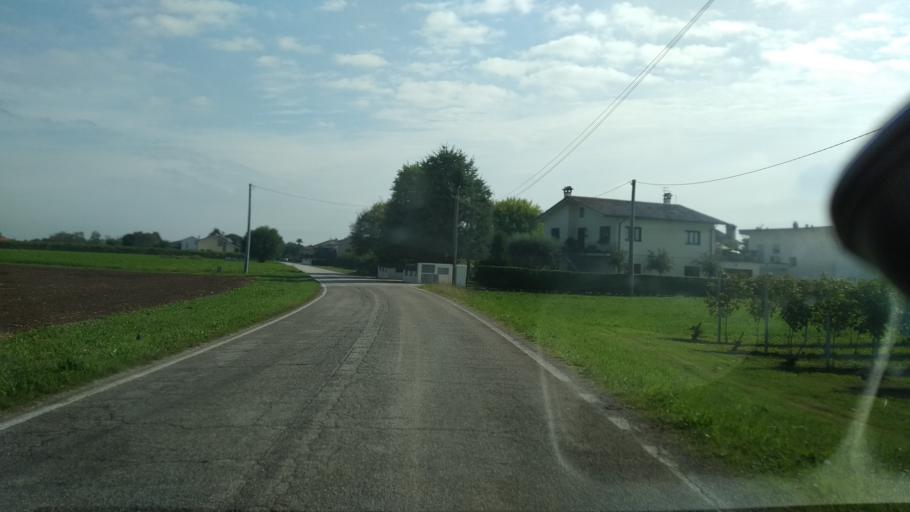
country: IT
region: Veneto
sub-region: Provincia di Vicenza
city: Breganze
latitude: 45.6982
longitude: 11.5700
